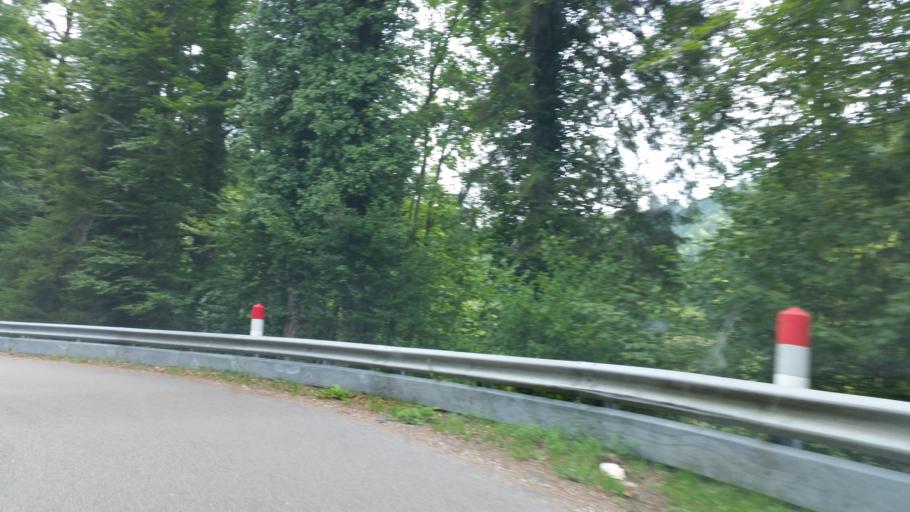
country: CH
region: Jura
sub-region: Franches-Montagnes District
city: Les Bois
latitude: 47.1631
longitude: 6.8545
